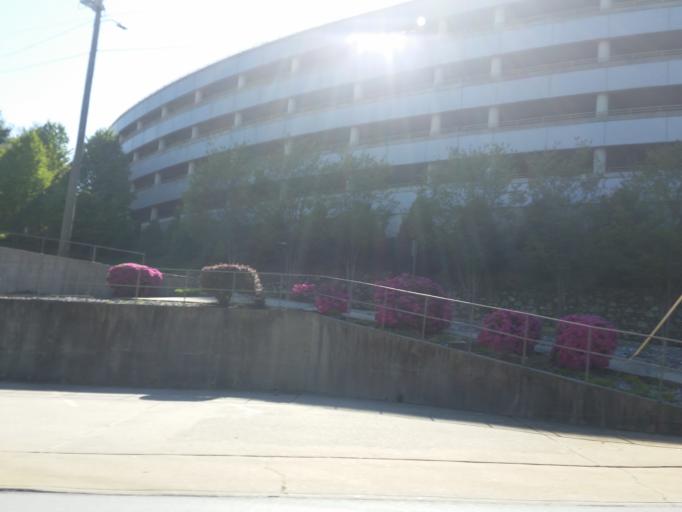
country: US
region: North Carolina
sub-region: Buncombe County
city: Asheville
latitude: 35.5758
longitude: -82.5471
